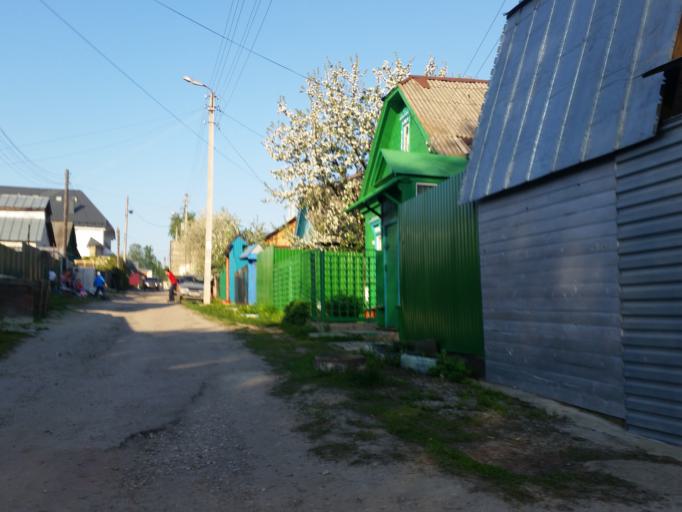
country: RU
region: Ulyanovsk
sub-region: Ulyanovskiy Rayon
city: Ulyanovsk
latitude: 54.3347
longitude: 48.3706
